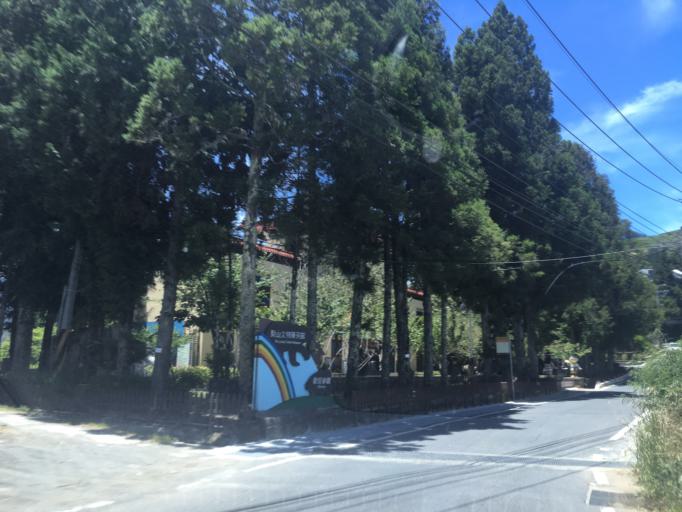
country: TW
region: Taiwan
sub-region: Nantou
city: Puli
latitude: 24.2529
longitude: 121.2567
